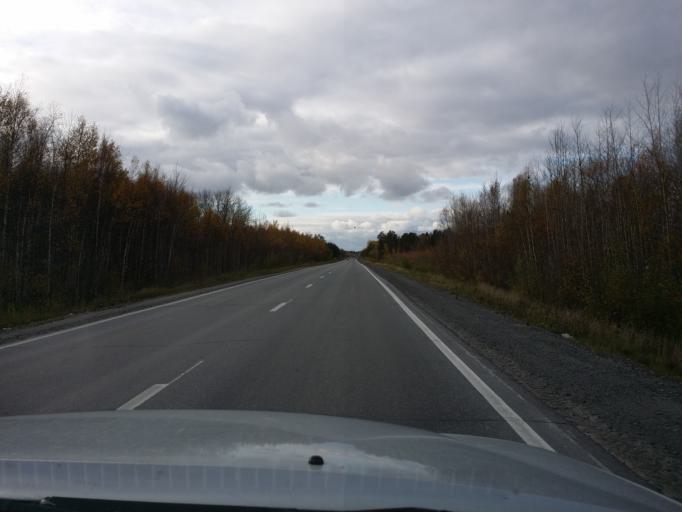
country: RU
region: Khanty-Mansiyskiy Avtonomnyy Okrug
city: Langepas
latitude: 61.2011
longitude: 75.4057
